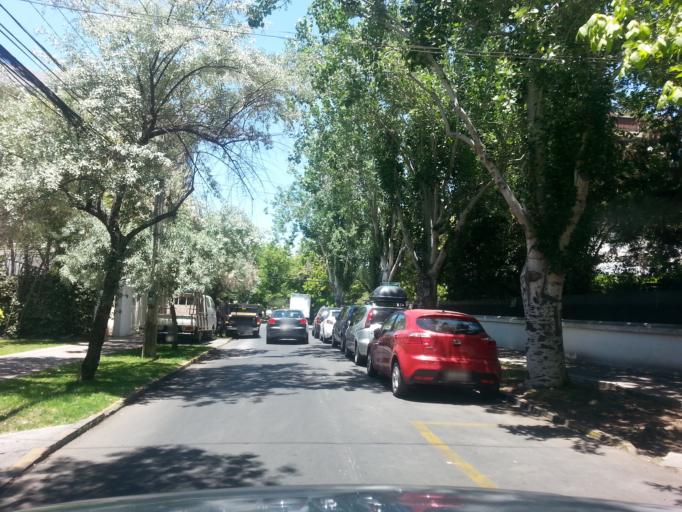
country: CL
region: Santiago Metropolitan
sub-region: Provincia de Santiago
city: Santiago
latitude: -33.4327
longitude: -70.6135
